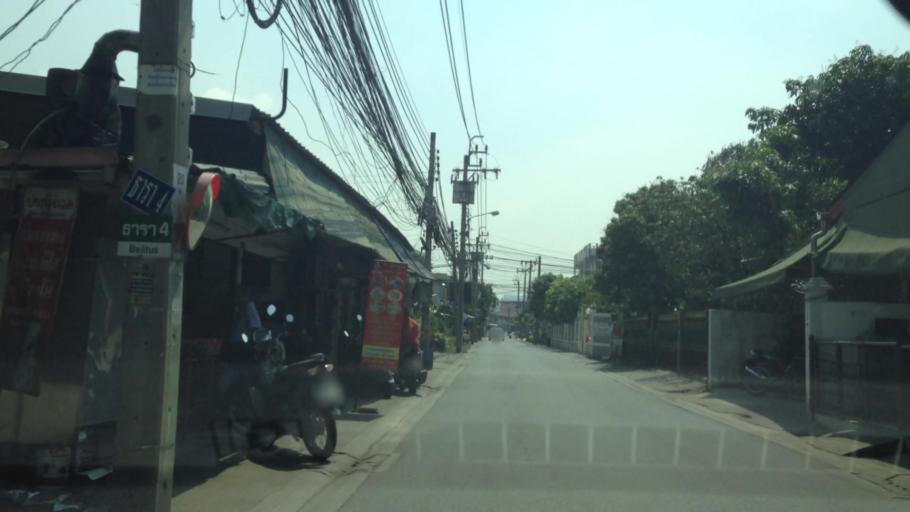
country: TH
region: Bangkok
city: Sai Mai
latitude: 13.9054
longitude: 100.6295
